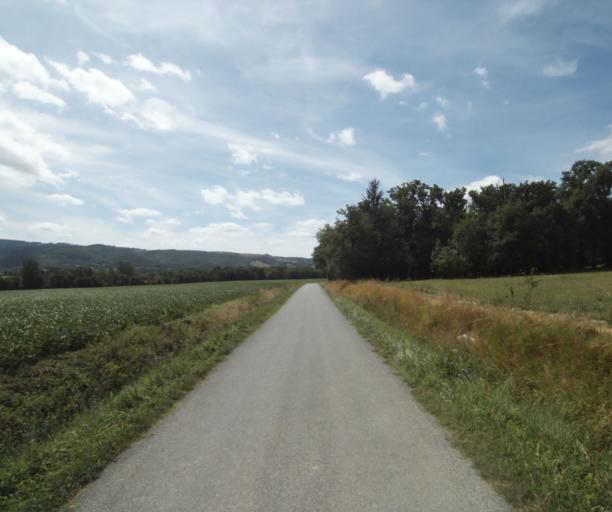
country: FR
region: Midi-Pyrenees
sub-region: Departement du Tarn
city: Soreze
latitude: 43.4805
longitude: 2.0767
